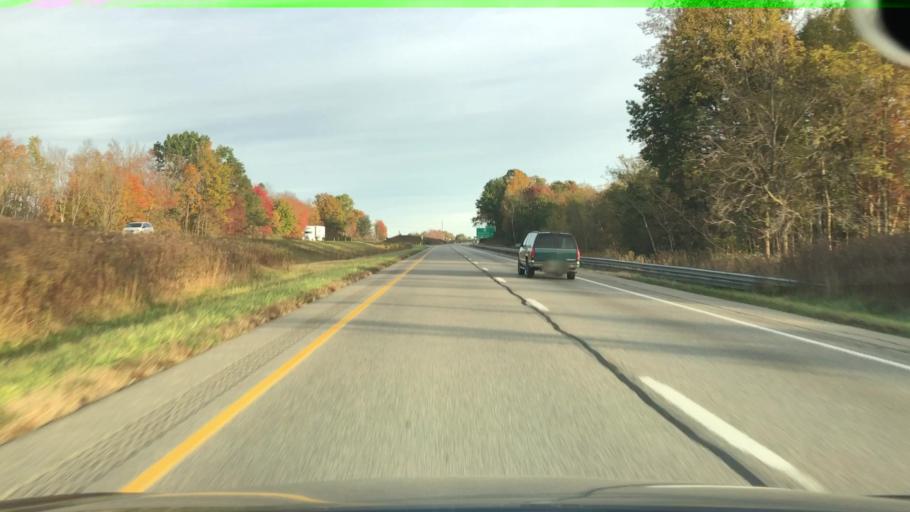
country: US
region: Pennsylvania
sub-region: Mercer County
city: Stoneboro
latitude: 41.3776
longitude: -80.1581
